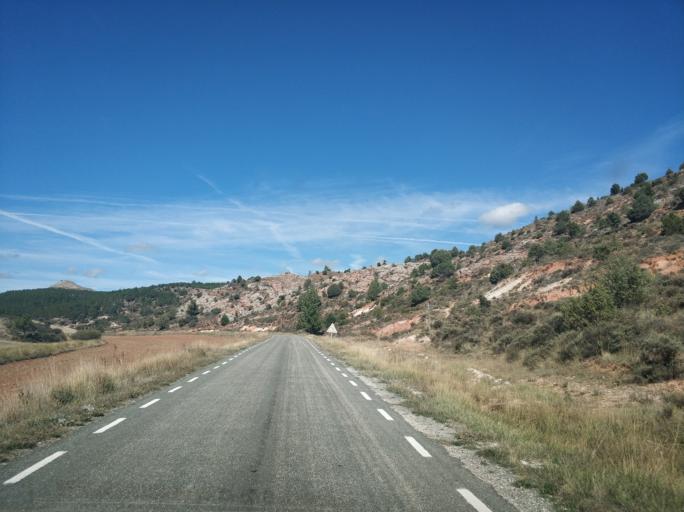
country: ES
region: Castille and Leon
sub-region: Provincia de Soria
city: Espeja de San Marcelino
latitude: 41.8107
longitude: -3.2240
